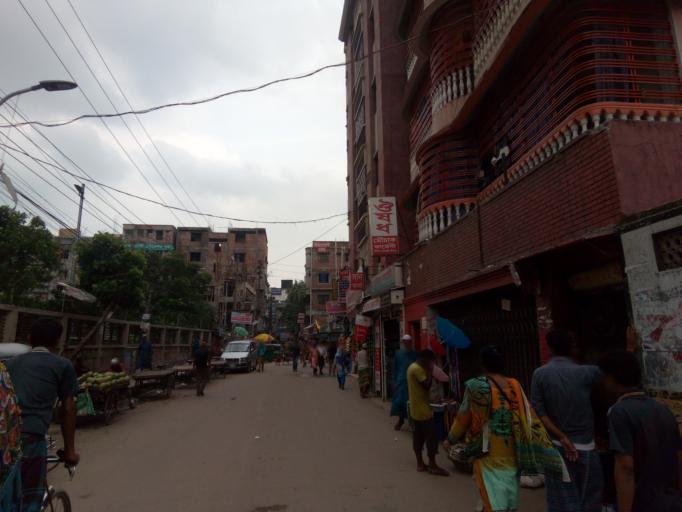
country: BD
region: Dhaka
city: Paltan
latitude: 23.7317
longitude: 90.4303
